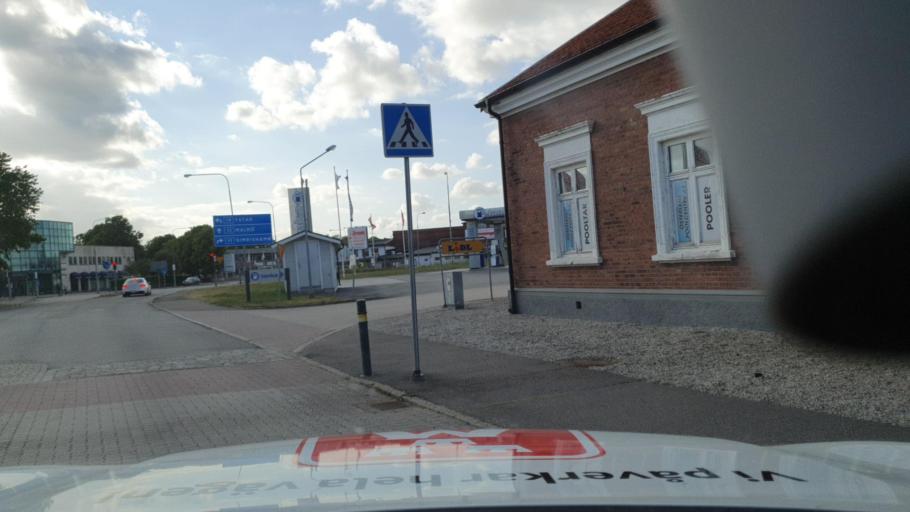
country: SE
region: Skane
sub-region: Tomelilla Kommun
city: Tomelilla
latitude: 55.5464
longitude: 13.9472
